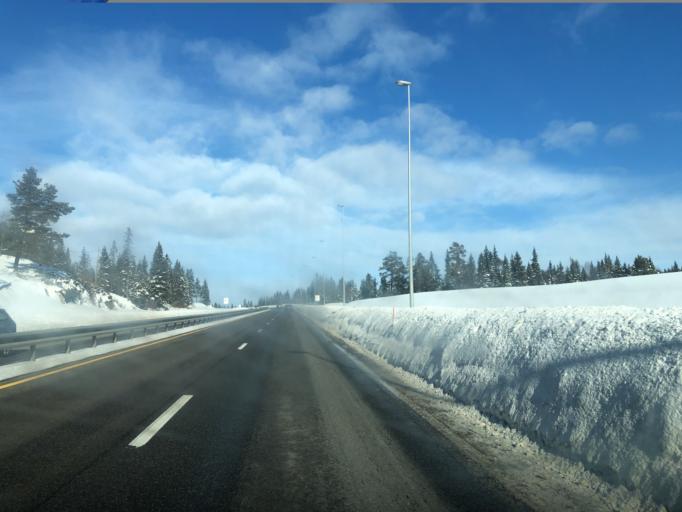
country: NO
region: Oppland
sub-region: Gran
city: Jaren
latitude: 60.4401
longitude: 10.6127
